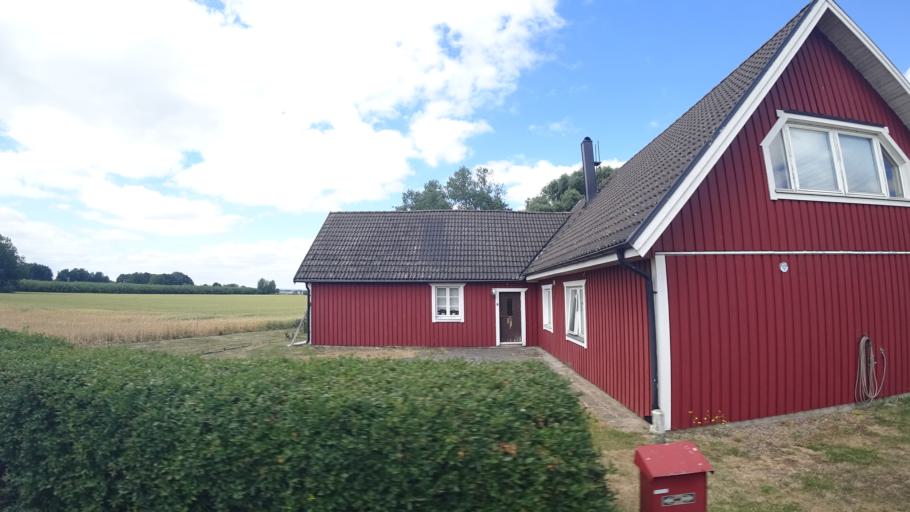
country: SE
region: Skane
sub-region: Kristianstads Kommun
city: Ahus
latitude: 55.9718
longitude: 14.2635
